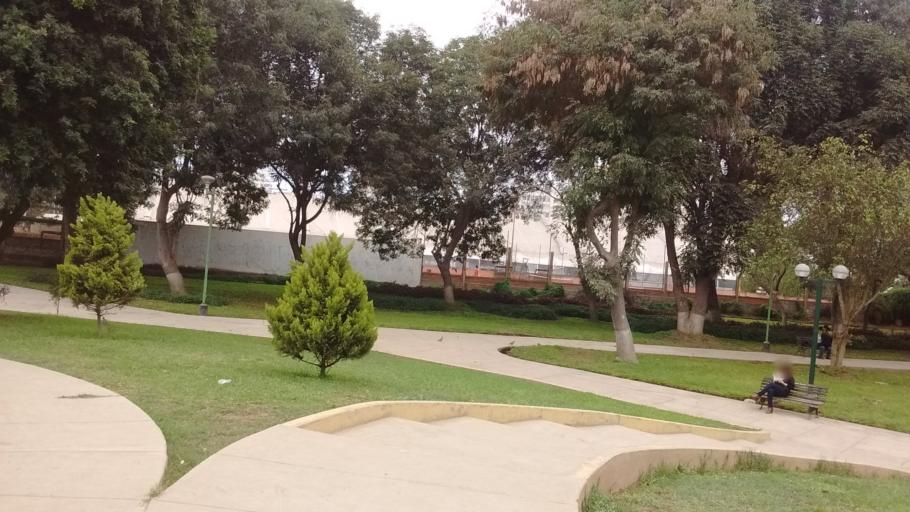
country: PE
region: Lima
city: Lima
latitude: -12.0691
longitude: -77.0436
